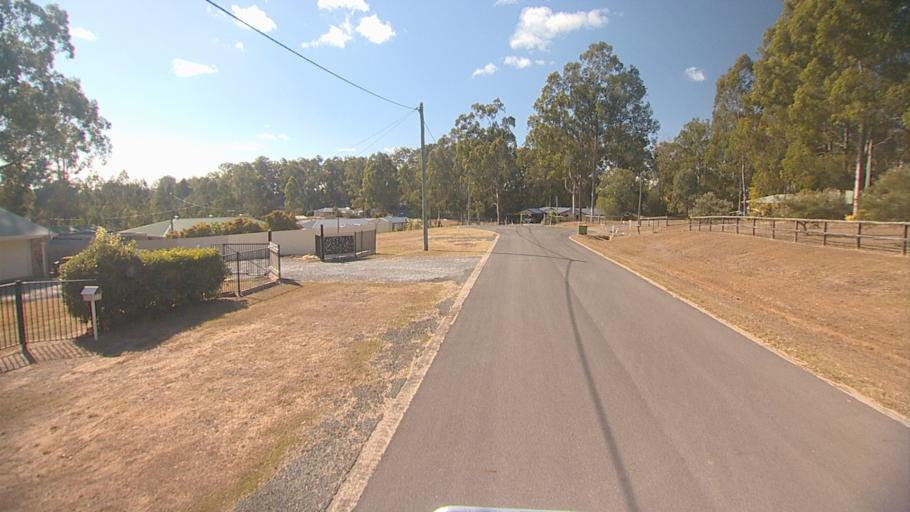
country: AU
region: Queensland
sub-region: Logan
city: Cedar Vale
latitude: -27.8783
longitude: 153.0071
